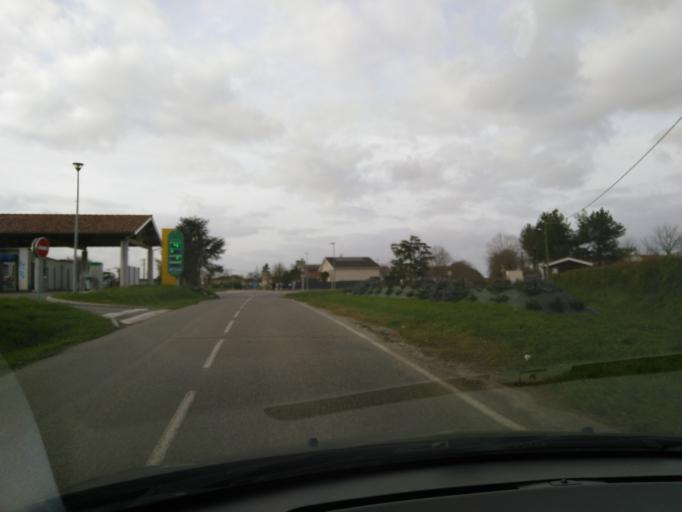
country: FR
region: Midi-Pyrenees
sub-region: Departement du Tarn-et-Garonne
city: Finhan
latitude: 43.8969
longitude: 1.1358
